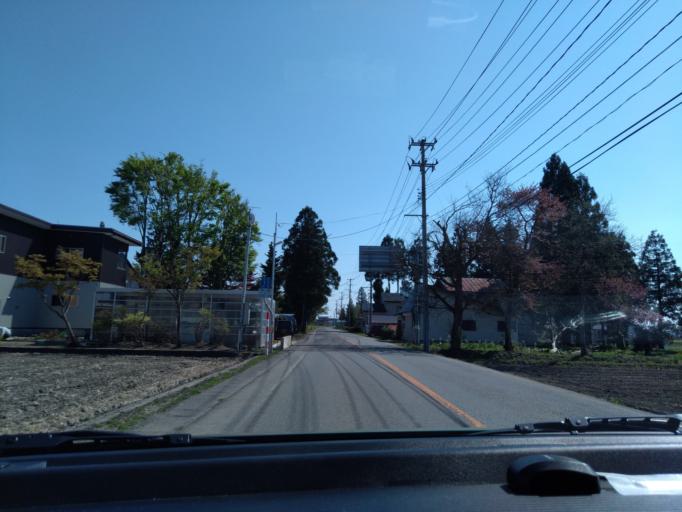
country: JP
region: Akita
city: Kakunodatemachi
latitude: 39.4889
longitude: 140.5927
